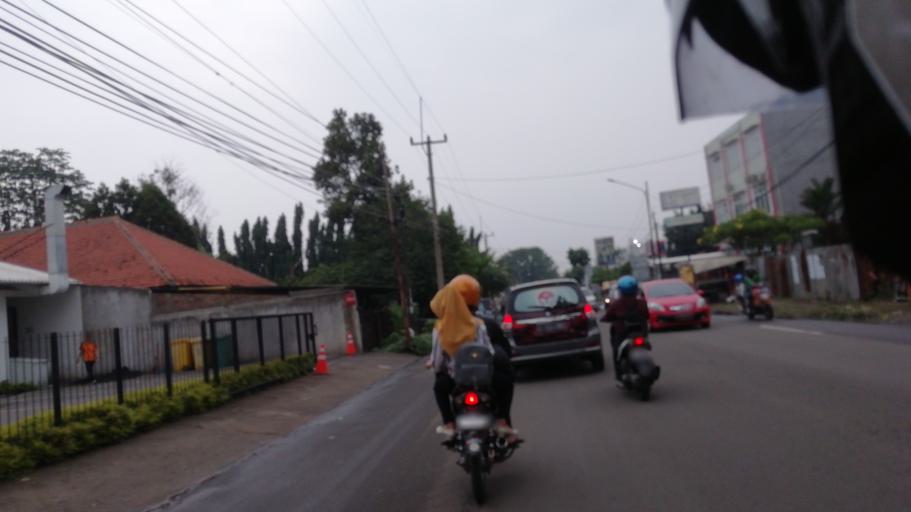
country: ID
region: West Java
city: Cibinong
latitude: -6.5094
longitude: 106.8069
